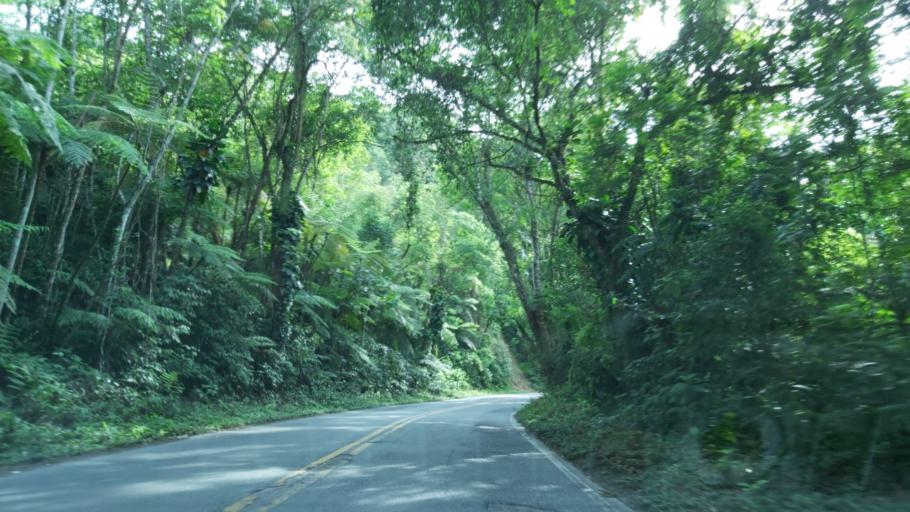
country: BR
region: Sao Paulo
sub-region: Juquia
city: Juquia
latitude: -24.0996
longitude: -47.6221
